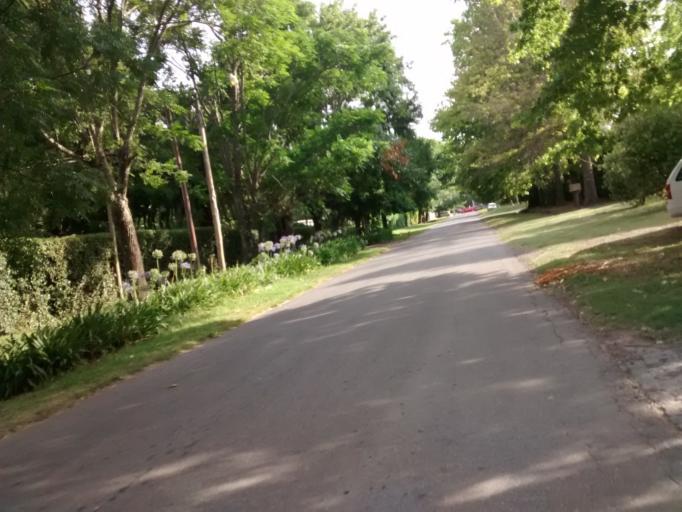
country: AR
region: Buenos Aires
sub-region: Partido de La Plata
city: La Plata
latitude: -34.8468
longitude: -58.0856
